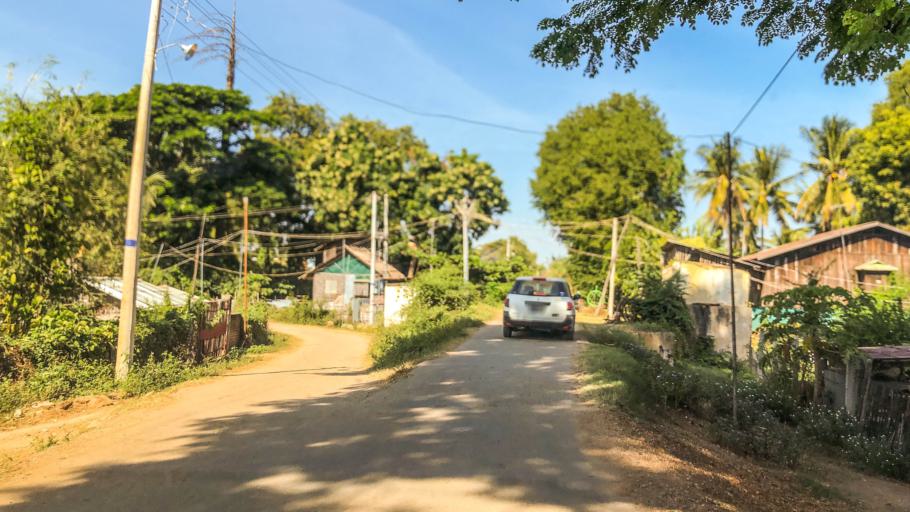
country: MM
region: Magway
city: Magway
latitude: 19.9719
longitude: 95.0414
